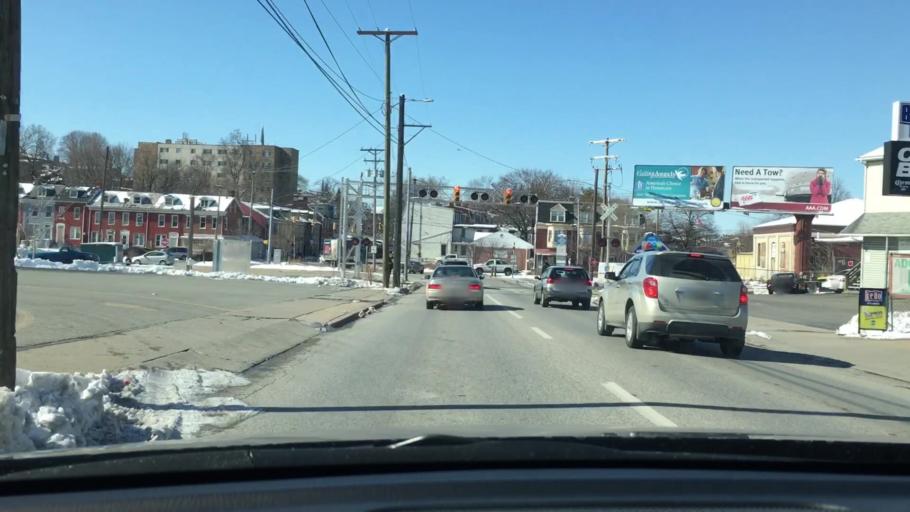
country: US
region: Pennsylvania
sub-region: York County
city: York
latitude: 39.9672
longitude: -76.7189
